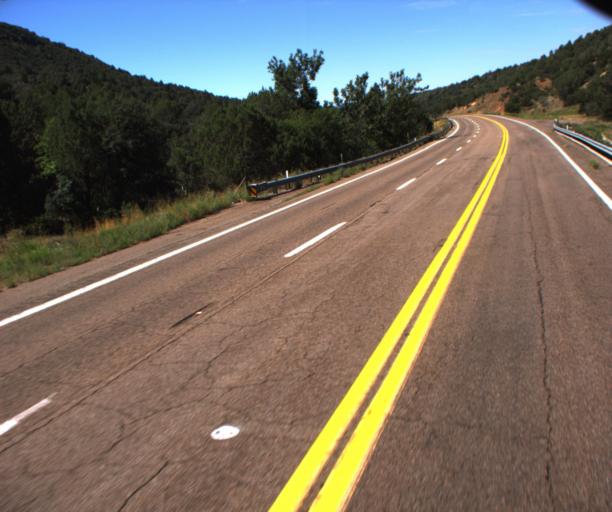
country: US
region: Arizona
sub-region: Navajo County
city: Cibecue
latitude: 33.8876
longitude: -110.3860
